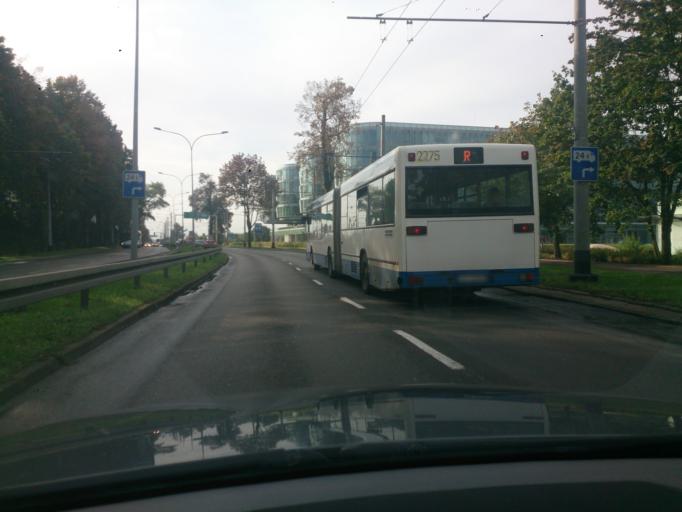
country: PL
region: Pomeranian Voivodeship
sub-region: Gdynia
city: Gdynia
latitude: 54.4948
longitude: 18.5391
